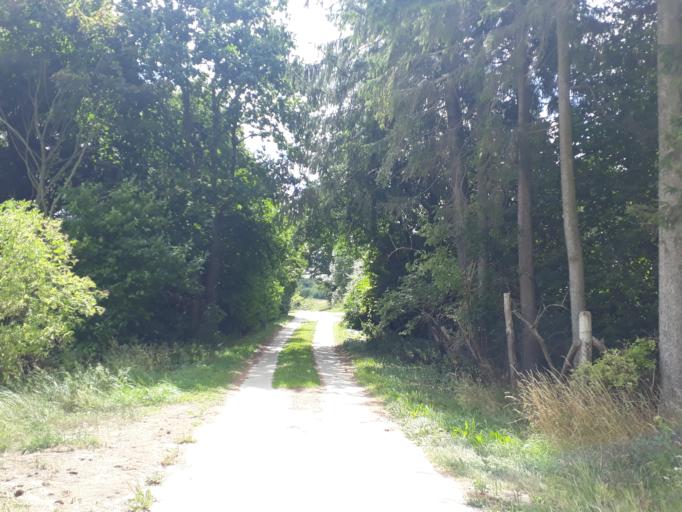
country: DE
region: Mecklenburg-Vorpommern
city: Marlow
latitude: 54.1754
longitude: 12.6051
